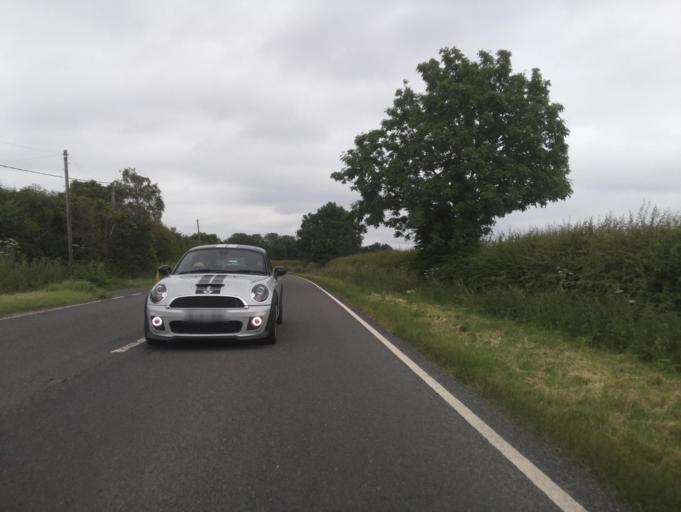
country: GB
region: England
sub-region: Nottinghamshire
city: East Leake
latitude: 52.8143
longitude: -1.1893
